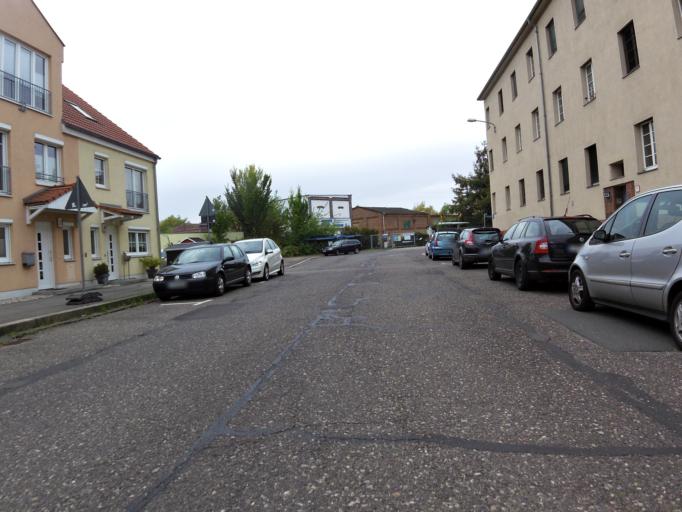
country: DE
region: Saxony
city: Leipzig
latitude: 51.3283
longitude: 12.3158
